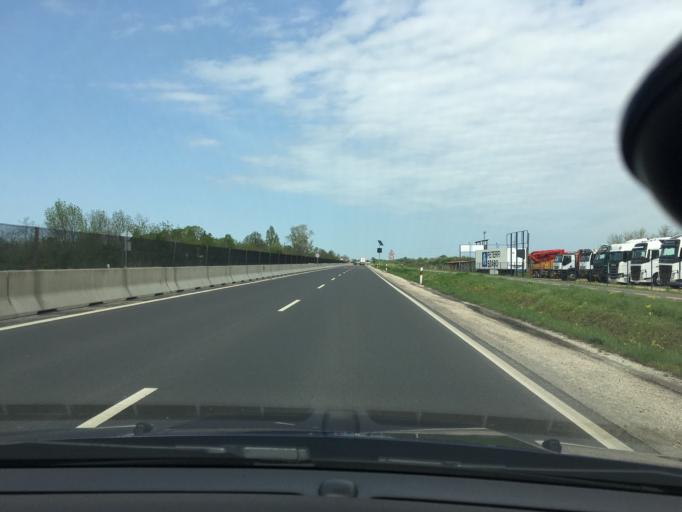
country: HU
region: Csongrad
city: Algyo
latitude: 46.2987
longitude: 20.1788
